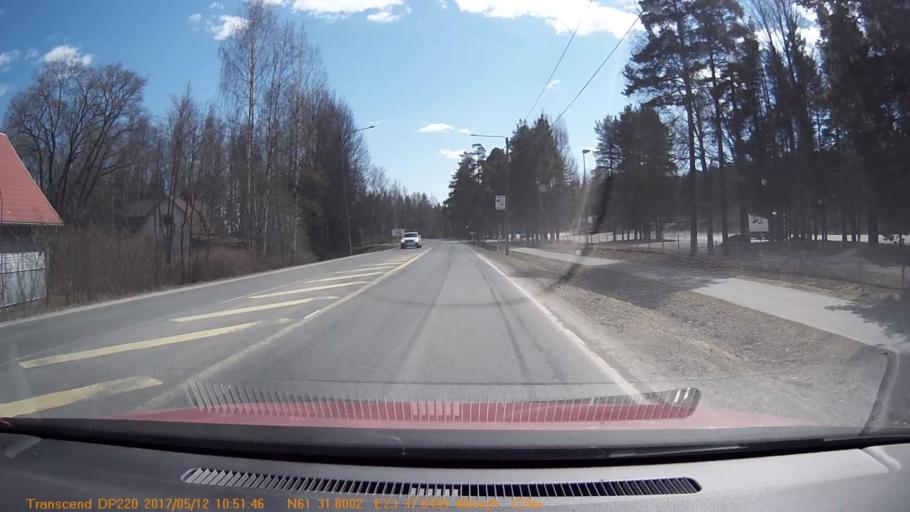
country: FI
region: Pirkanmaa
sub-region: Tampere
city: Yloejaervi
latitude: 61.5299
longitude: 23.6309
